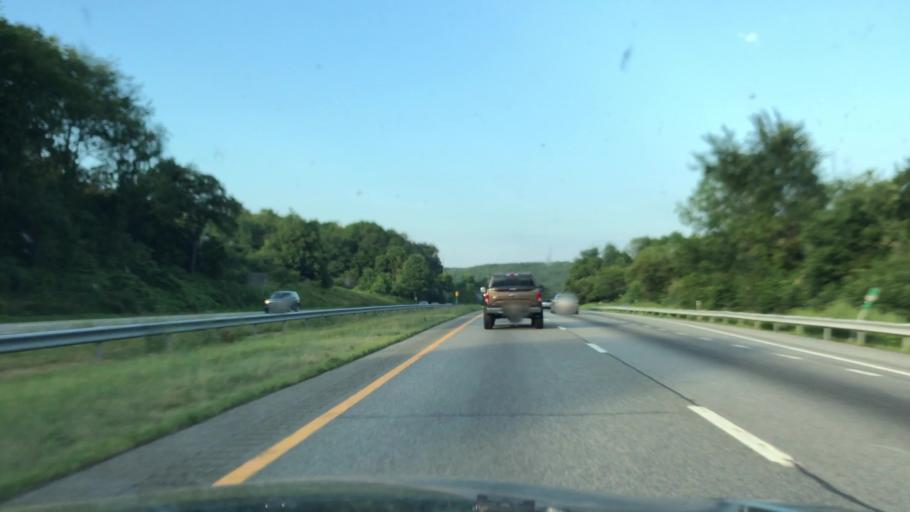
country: US
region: New York
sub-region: Orange County
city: Monroe
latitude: 41.3468
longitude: -74.2075
